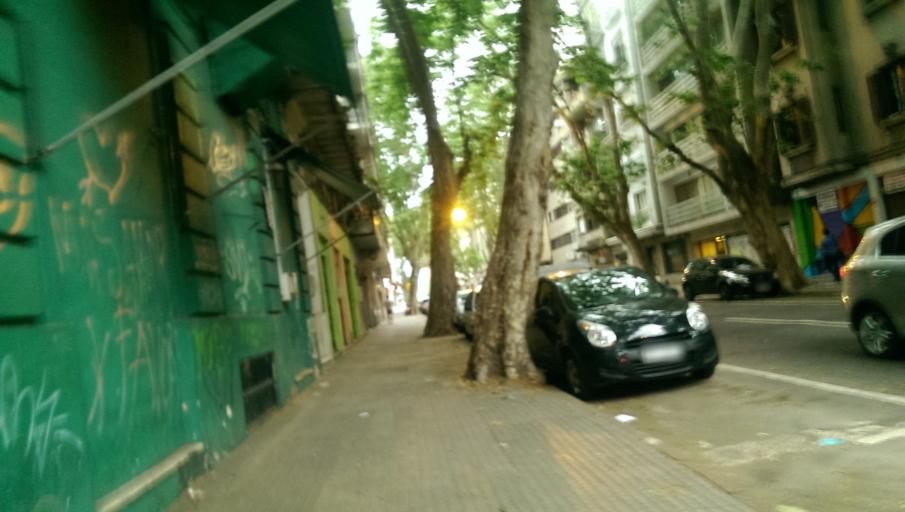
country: UY
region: Montevideo
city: Montevideo
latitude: -34.9082
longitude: -56.1959
